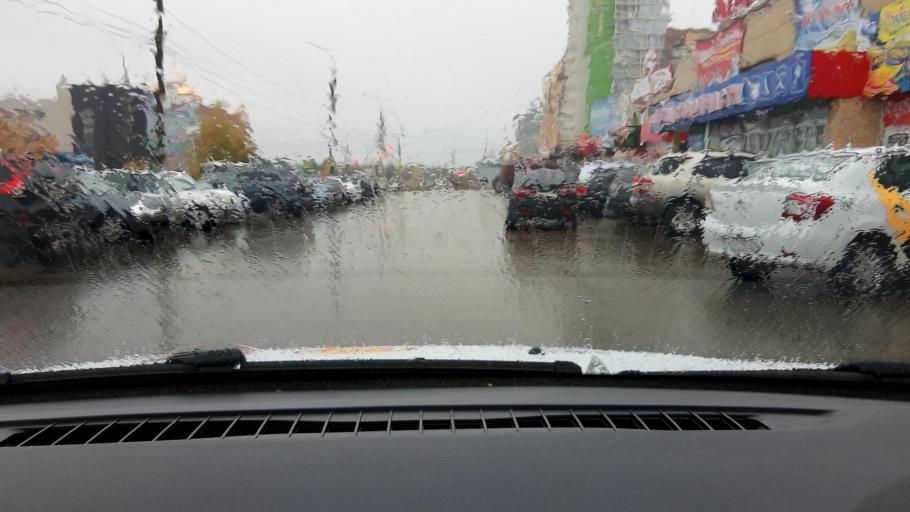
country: RU
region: Nizjnij Novgorod
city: Dzerzhinsk
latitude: 56.2319
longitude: 43.4096
